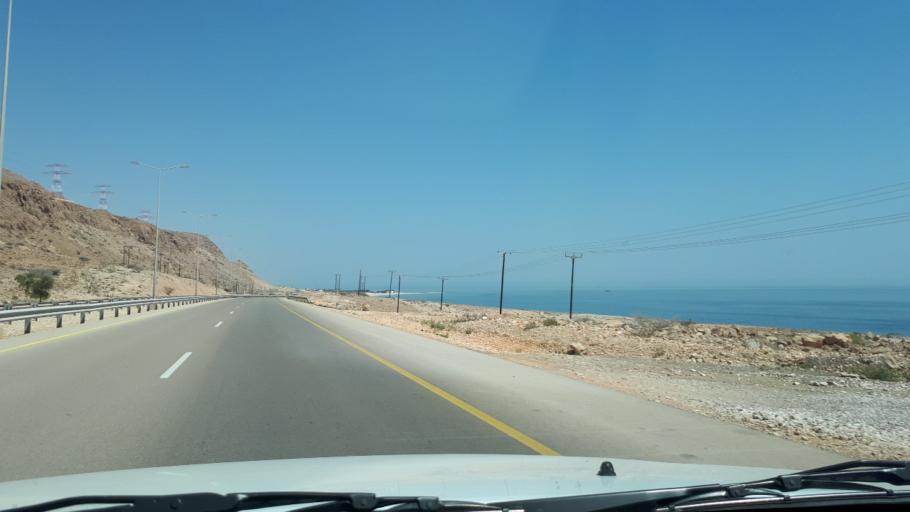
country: OM
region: Ash Sharqiyah
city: Sur
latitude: 22.8029
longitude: 59.2693
